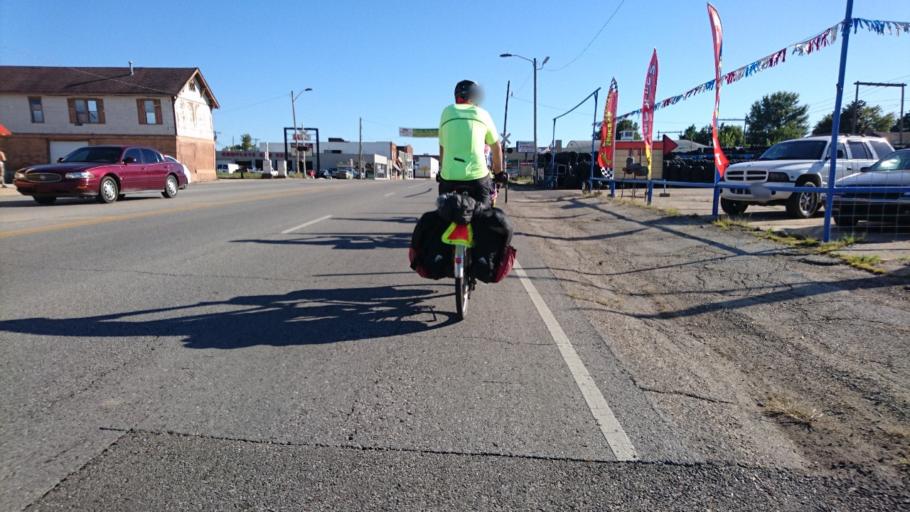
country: US
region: Oklahoma
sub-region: Ottawa County
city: Miami
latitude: 36.8807
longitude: -94.8776
